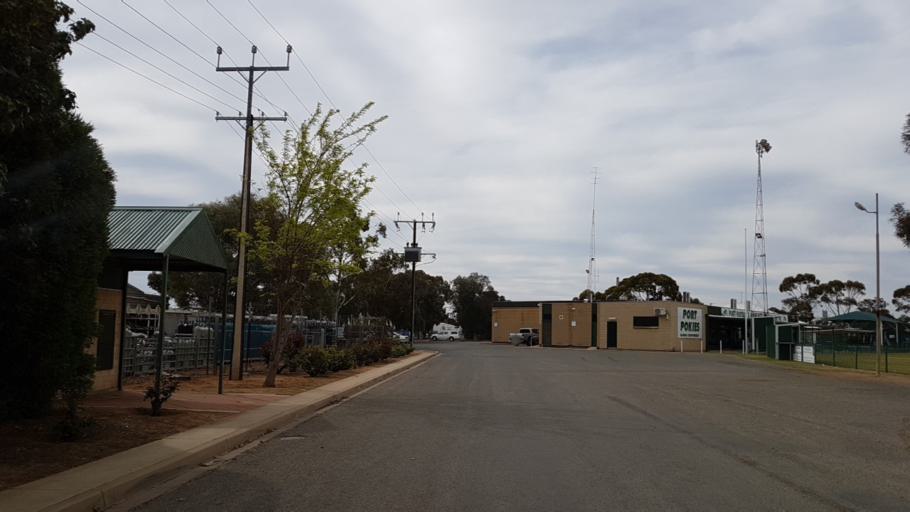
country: AU
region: South Australia
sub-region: Port Pirie City and Dists
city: Port Pirie
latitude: -33.1928
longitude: 138.0082
